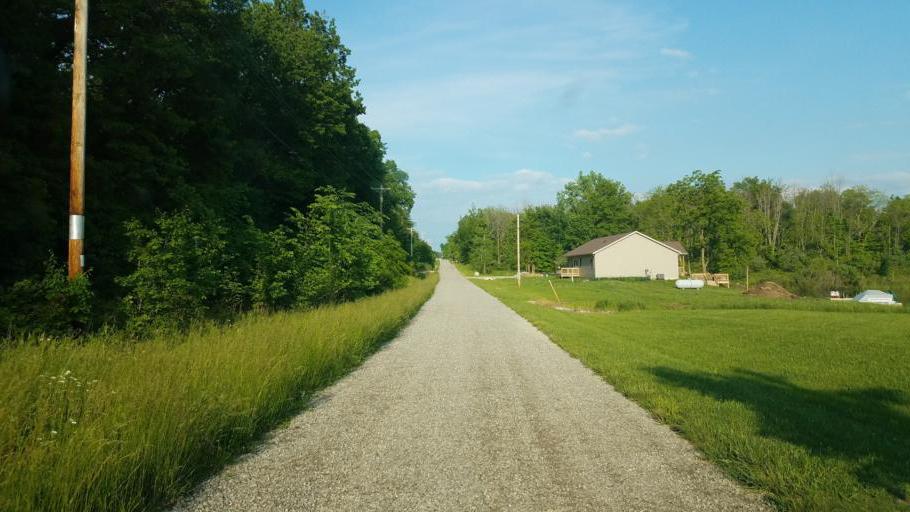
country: US
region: Ohio
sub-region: Morrow County
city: Cardington
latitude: 40.4251
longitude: -82.8175
